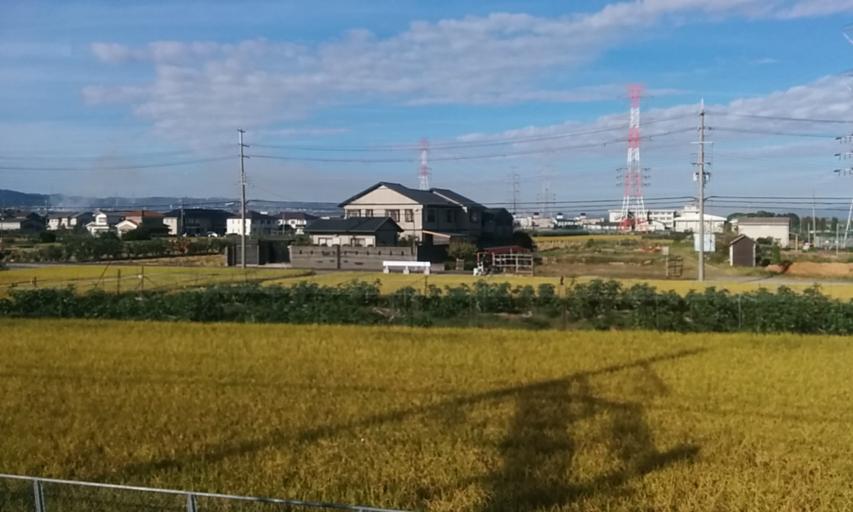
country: JP
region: Kyoto
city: Tanabe
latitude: 34.8427
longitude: 135.7726
